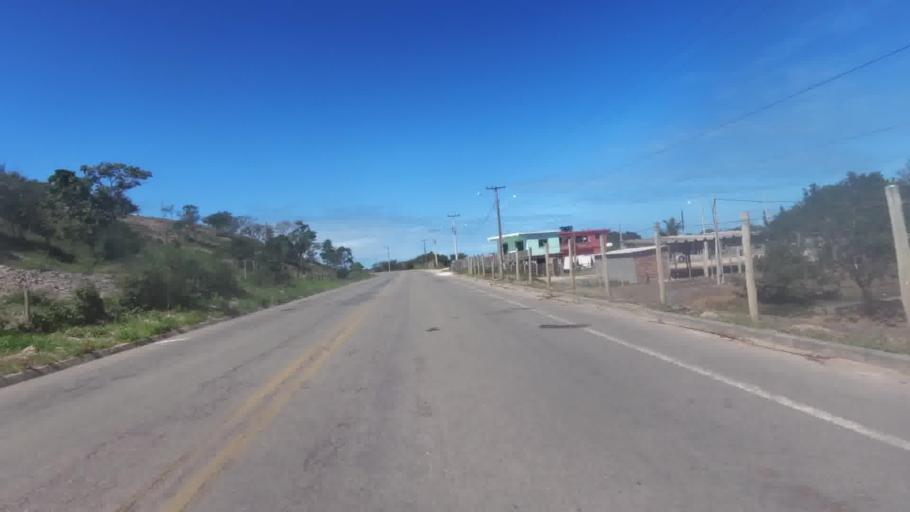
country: BR
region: Espirito Santo
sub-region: Marataizes
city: Marataizes
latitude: -21.1995
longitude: -40.9495
